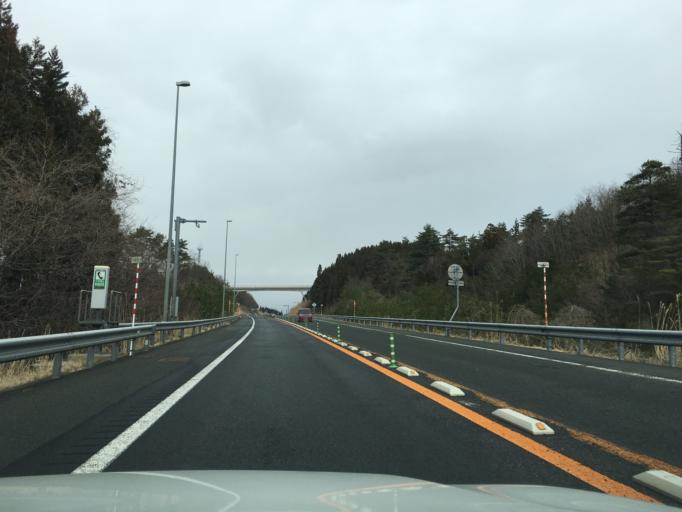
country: JP
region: Akita
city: Tenno
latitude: 40.0033
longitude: 140.0909
